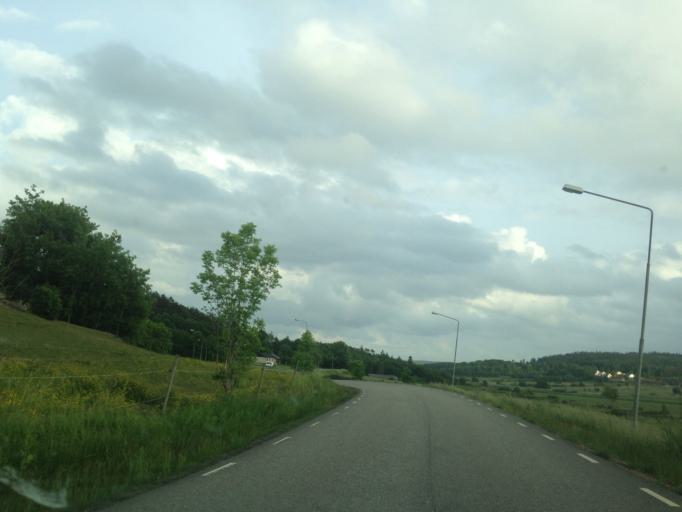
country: SE
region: Vaestra Goetaland
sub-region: Kungalvs Kommun
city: Kungalv
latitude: 57.7970
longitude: 11.9233
